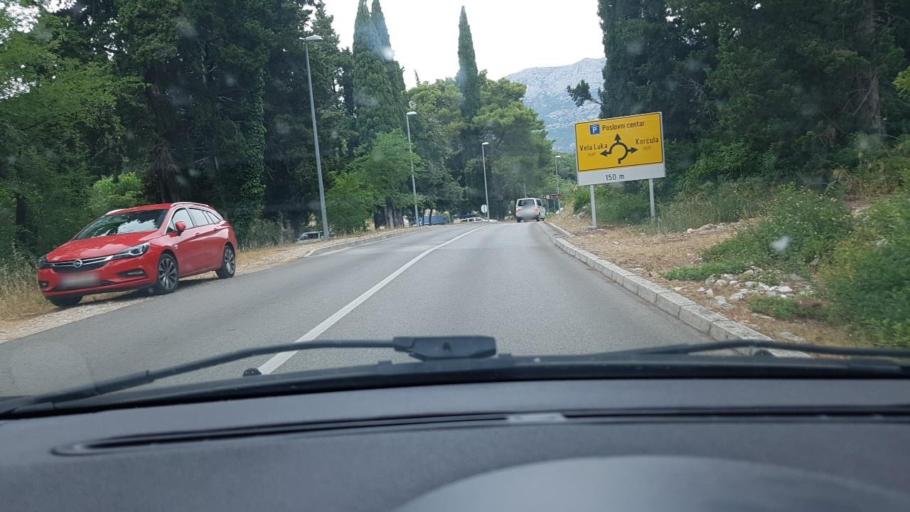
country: HR
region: Dubrovacko-Neretvanska
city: Korcula
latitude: 42.9544
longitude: 17.1313
